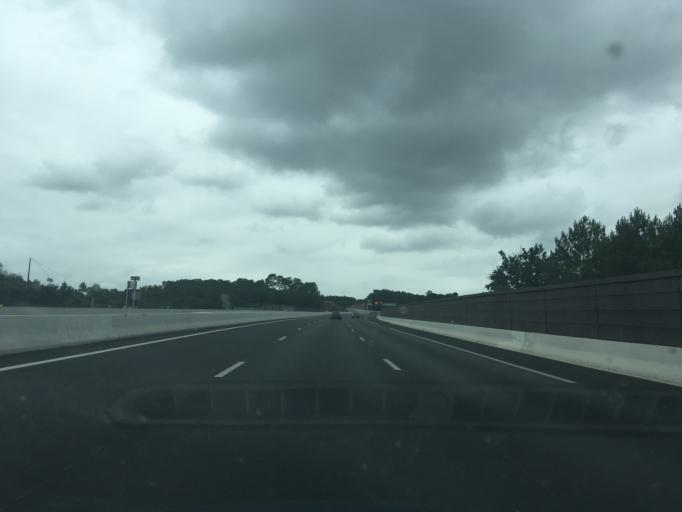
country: FR
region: Aquitaine
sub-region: Departement des Landes
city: Labenne
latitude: 43.5794
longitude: -1.4235
